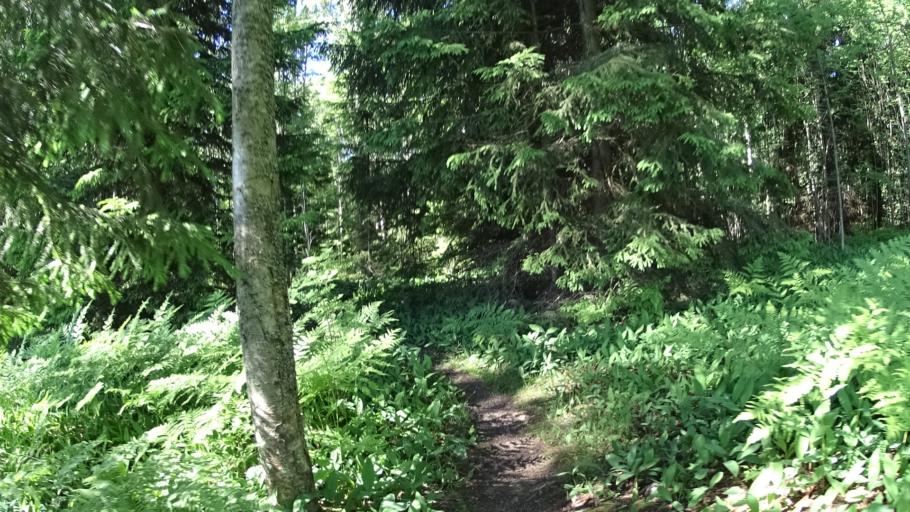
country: FI
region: Uusimaa
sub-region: Helsinki
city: Kilo
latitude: 60.2984
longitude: 24.8419
